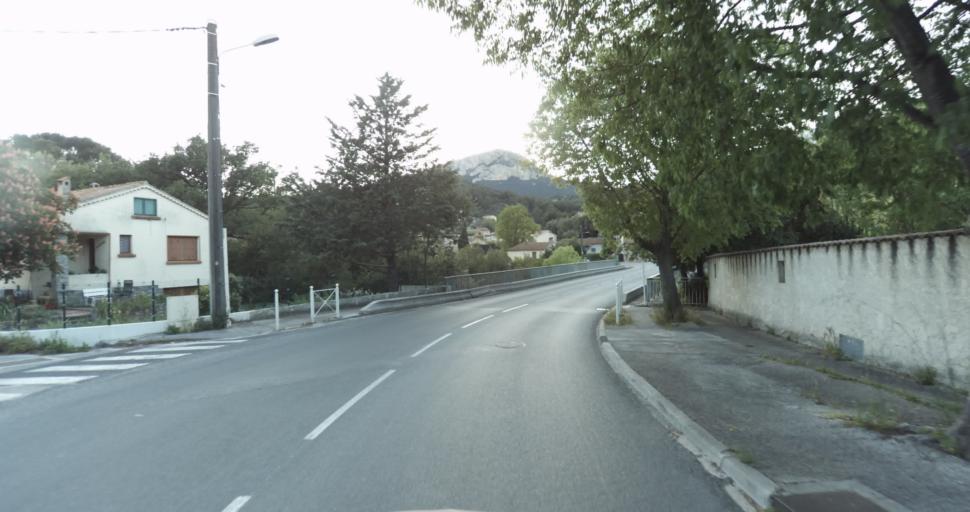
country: FR
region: Provence-Alpes-Cote d'Azur
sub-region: Departement du Var
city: Le Revest-les-Eaux
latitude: 43.1592
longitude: 5.9211
